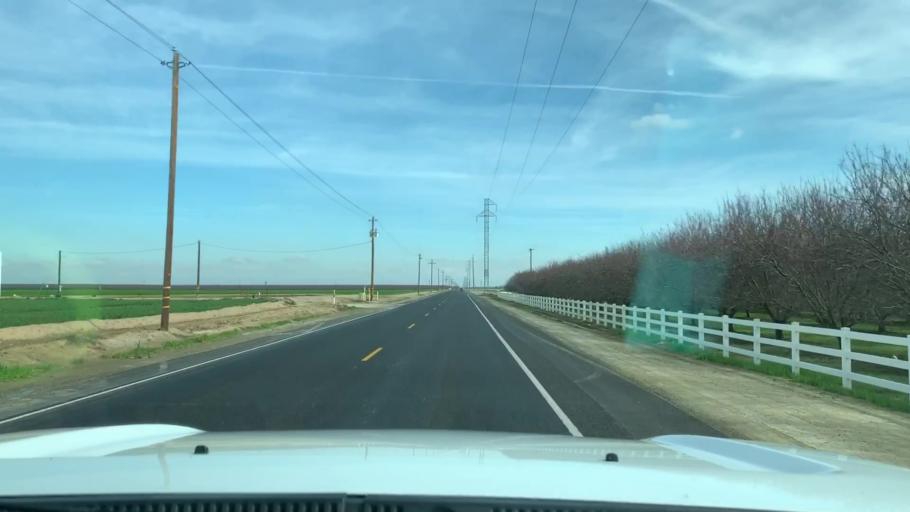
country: US
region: California
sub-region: Kern County
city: Shafter
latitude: 35.4420
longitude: -119.3424
